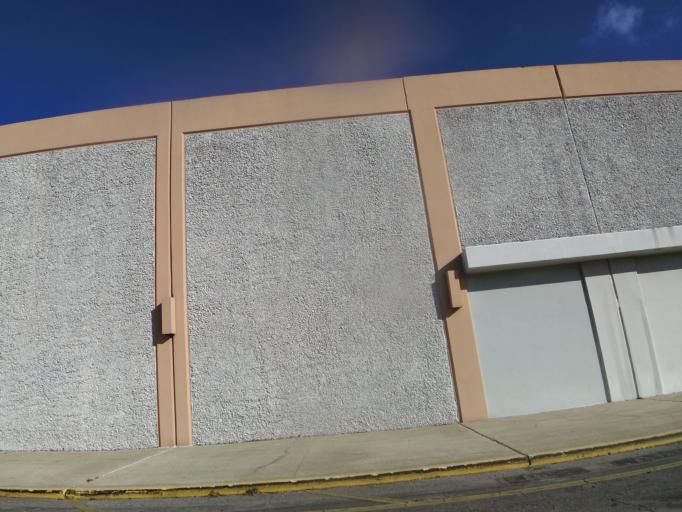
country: US
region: Florida
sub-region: Duval County
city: Jacksonville
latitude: 30.3215
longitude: -81.5445
